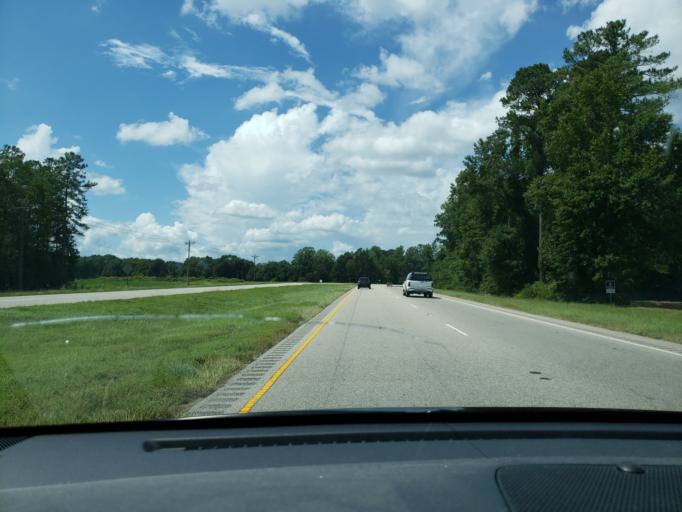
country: US
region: North Carolina
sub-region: Bladen County
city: Elizabethtown
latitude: 34.7227
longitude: -78.7626
